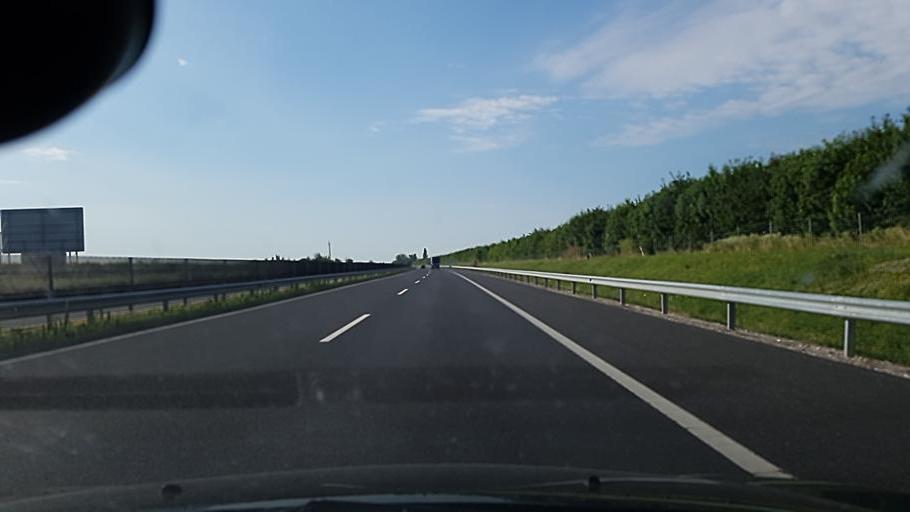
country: HU
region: Fejer
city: Ivancsa
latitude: 47.1405
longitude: 18.8101
